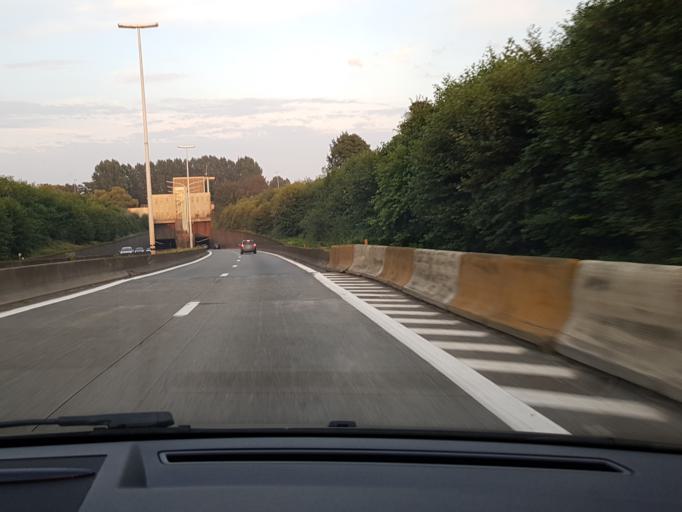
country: BE
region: Flanders
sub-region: Provincie Oost-Vlaanderen
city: Zelzate
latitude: 51.1929
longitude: 3.7939
